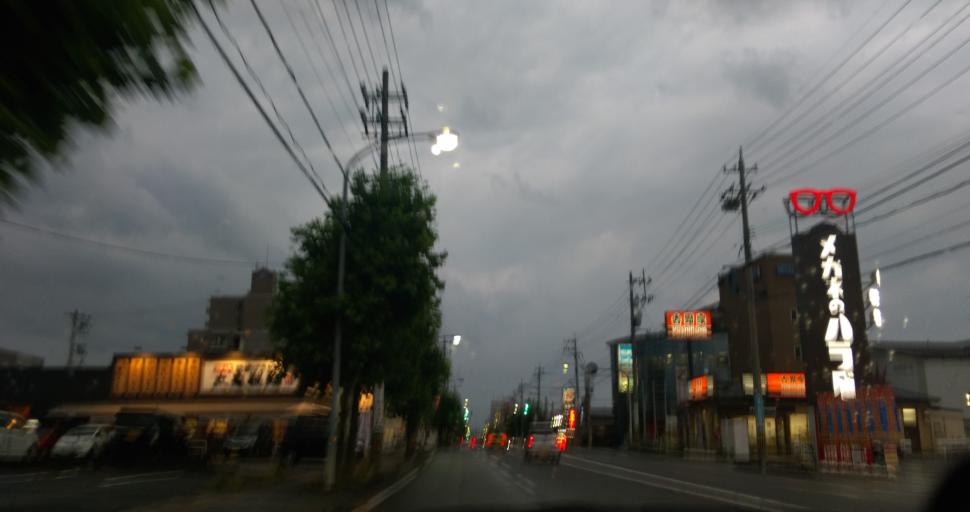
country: JP
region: Fukui
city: Fukui-shi
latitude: 36.0403
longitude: 136.2143
